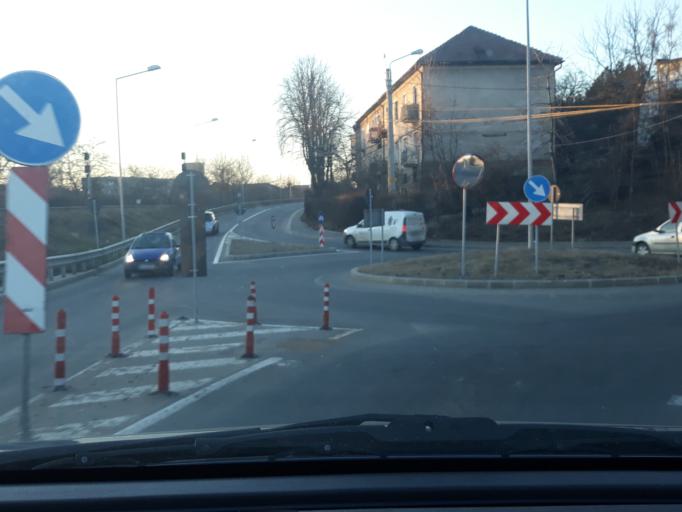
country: RO
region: Bihor
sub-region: Comuna Biharea
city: Oradea
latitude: 47.0623
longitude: 21.9416
